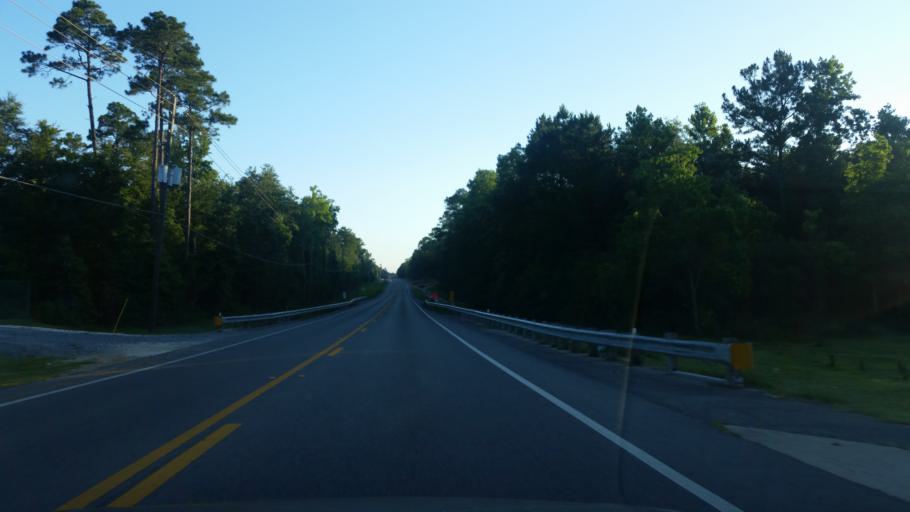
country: US
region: Florida
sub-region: Escambia County
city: Cantonment
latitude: 30.5823
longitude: -87.3283
